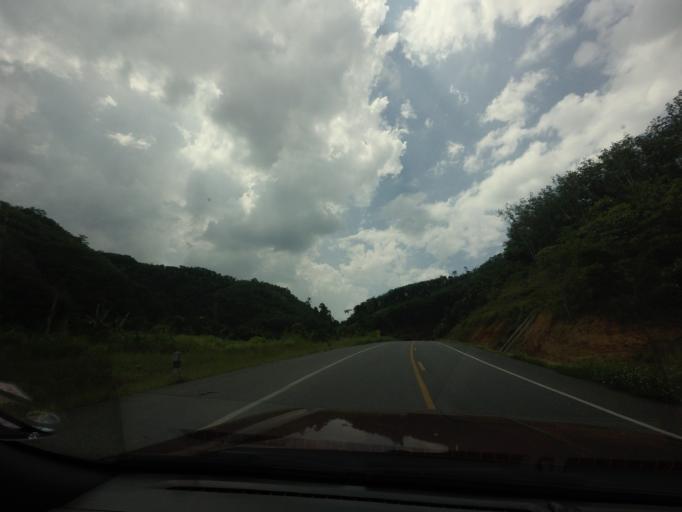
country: TH
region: Yala
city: Than To
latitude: 6.0586
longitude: 101.1942
